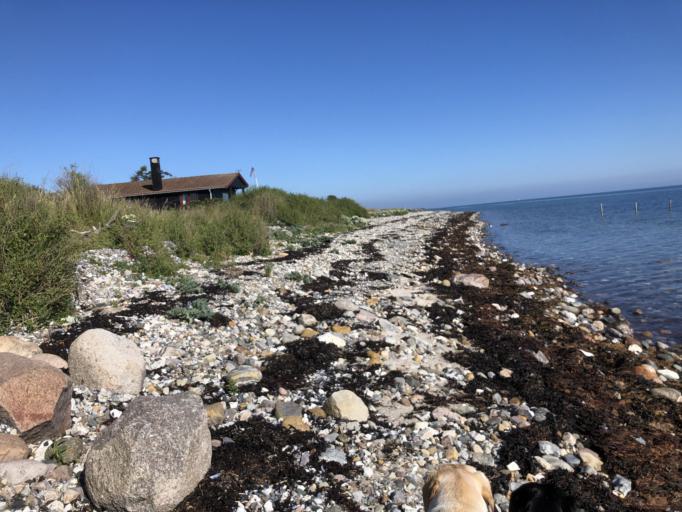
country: DK
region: Zealand
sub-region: Slagelse Kommune
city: Skaelskor
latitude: 55.1983
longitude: 11.1752
